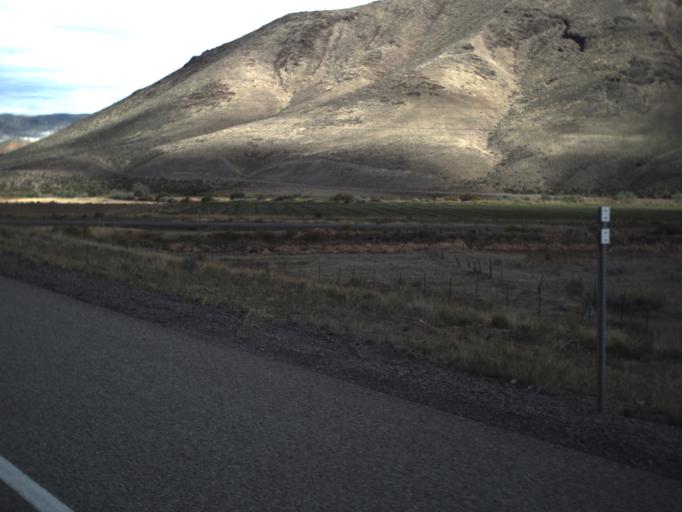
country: US
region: Utah
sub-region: Sevier County
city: Aurora
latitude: 38.8748
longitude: -111.9620
